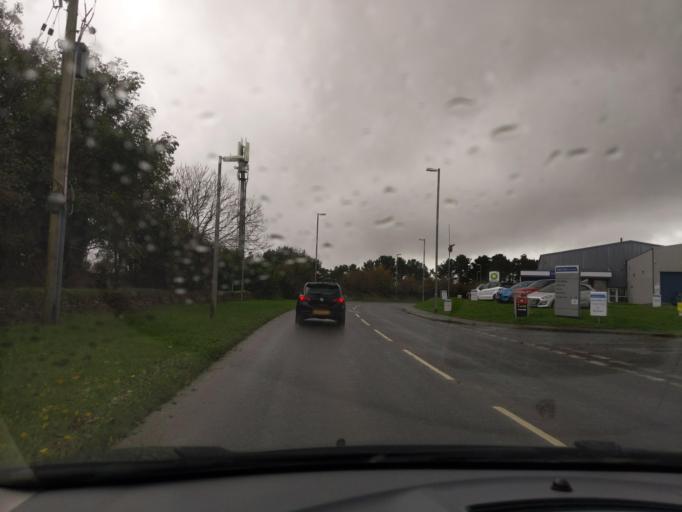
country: GB
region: England
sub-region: Cornwall
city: Wadebridge
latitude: 50.5174
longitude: -4.8574
